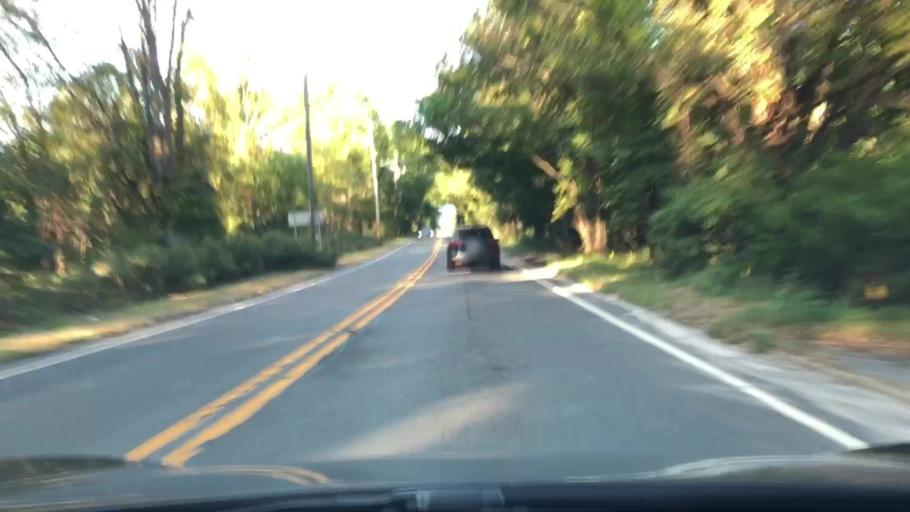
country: US
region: New Jersey
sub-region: Mercer County
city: Lawrenceville
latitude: 40.3141
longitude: -74.7064
